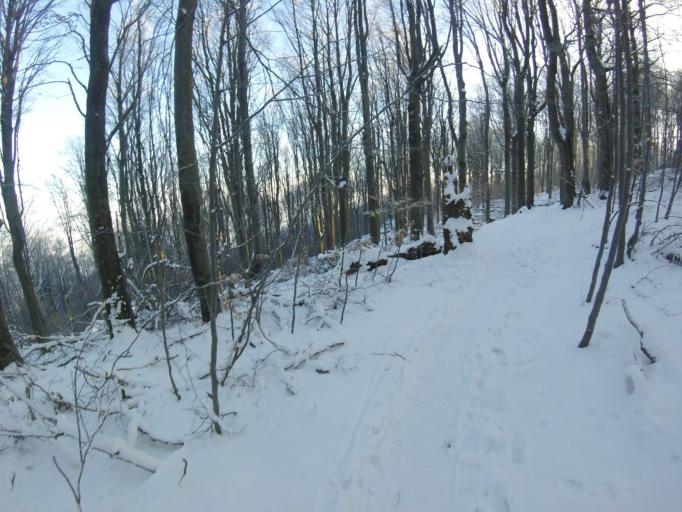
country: HU
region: Heves
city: Paradsasvar
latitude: 47.8732
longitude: 20.0099
